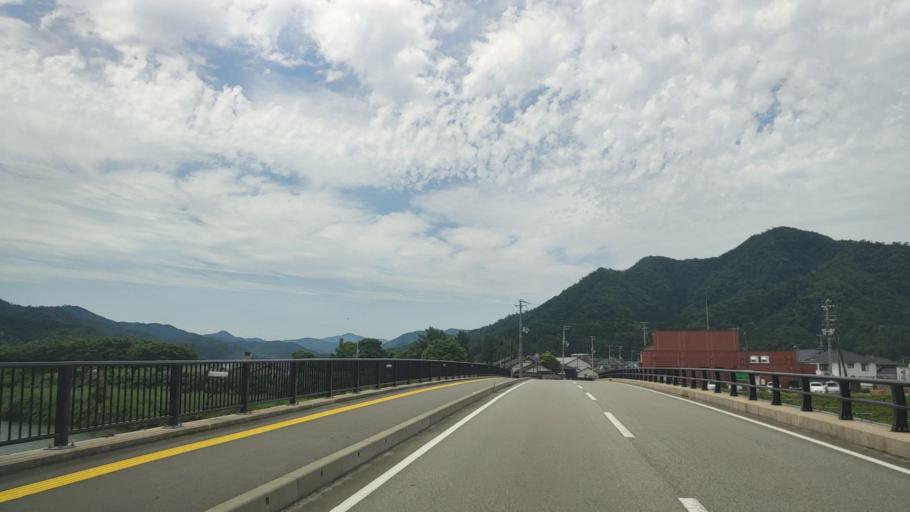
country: JP
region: Hyogo
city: Toyooka
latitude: 35.6543
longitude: 134.7607
